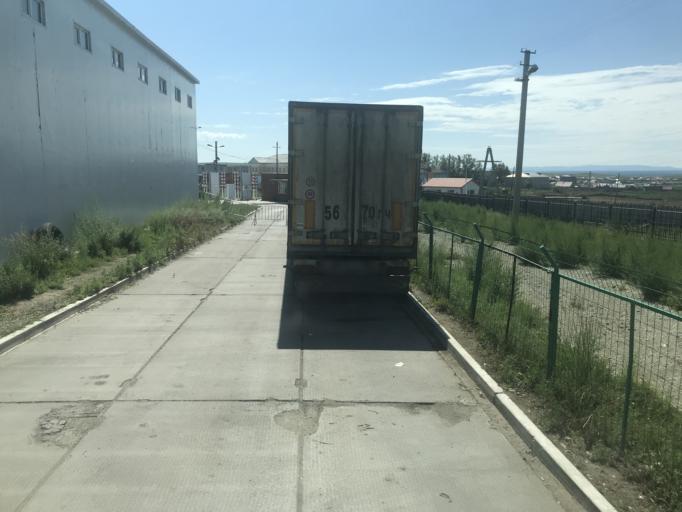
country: MN
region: Selenge
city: Altanbulag
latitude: 50.3209
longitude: 106.4892
